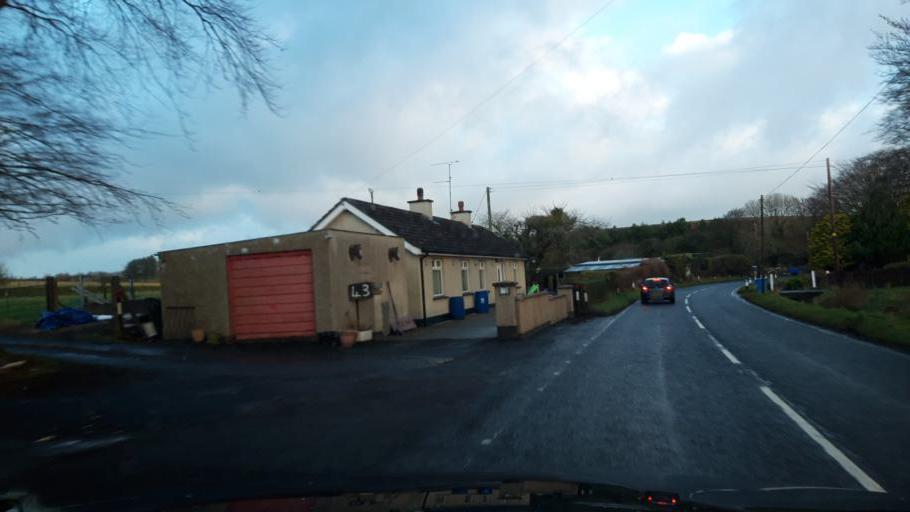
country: GB
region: Northern Ireland
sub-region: Moyle District
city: Ballycastle
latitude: 55.1774
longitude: -6.3009
